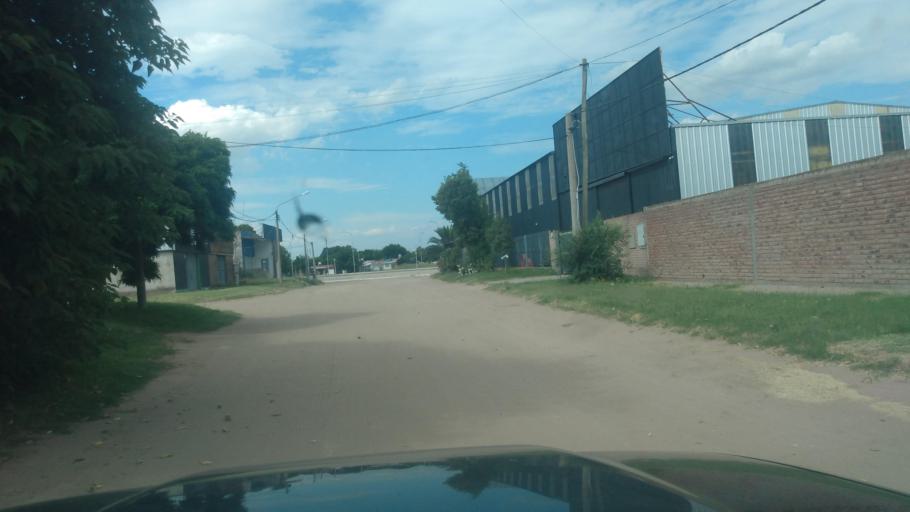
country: AR
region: La Pampa
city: Santa Rosa
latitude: -36.6430
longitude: -64.2835
